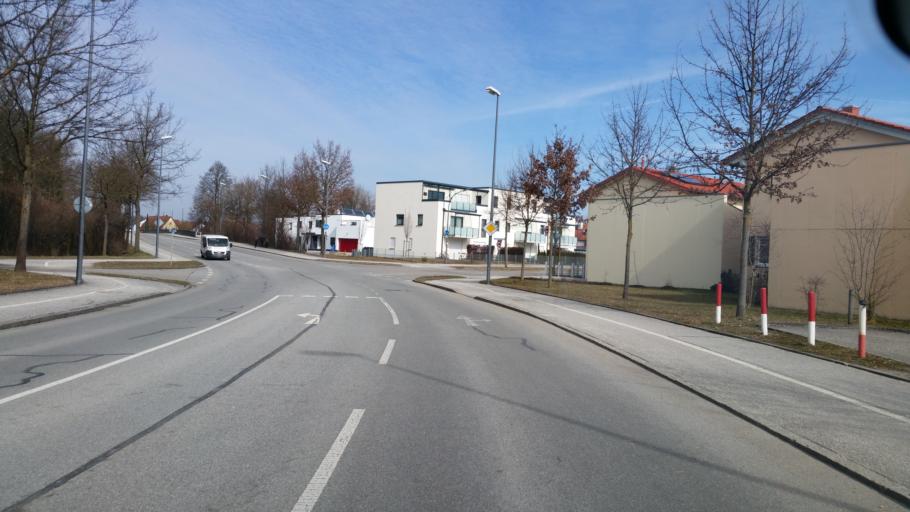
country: DE
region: Bavaria
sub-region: Lower Bavaria
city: Landshut
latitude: 48.5403
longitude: 12.1193
